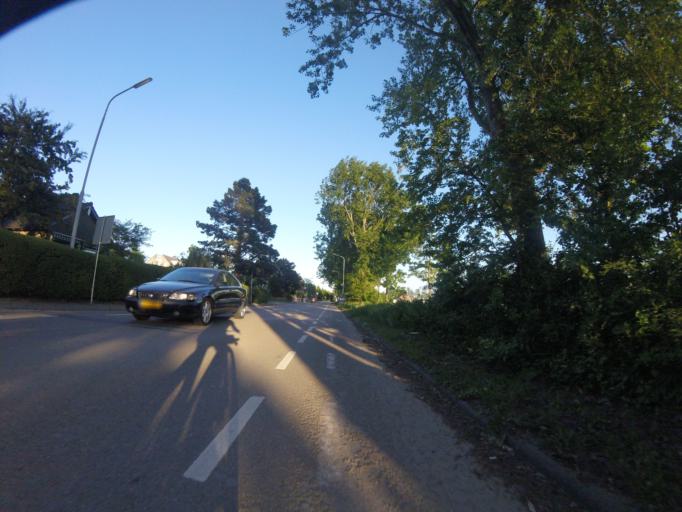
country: NL
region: North Holland
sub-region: Gemeente Haarlemmermeer
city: Hoofddorp
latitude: 52.3747
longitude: 4.7439
